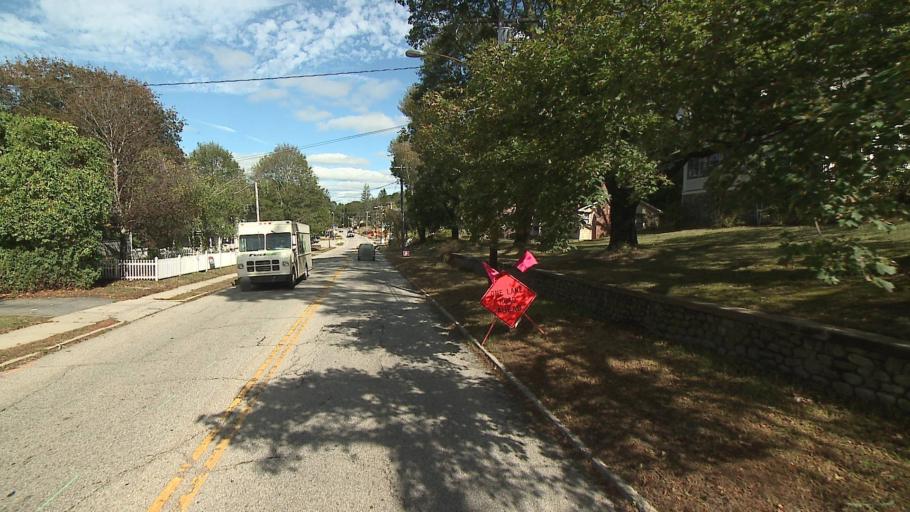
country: US
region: Connecticut
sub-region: Windham County
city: Danielson
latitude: 41.8145
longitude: -71.8766
